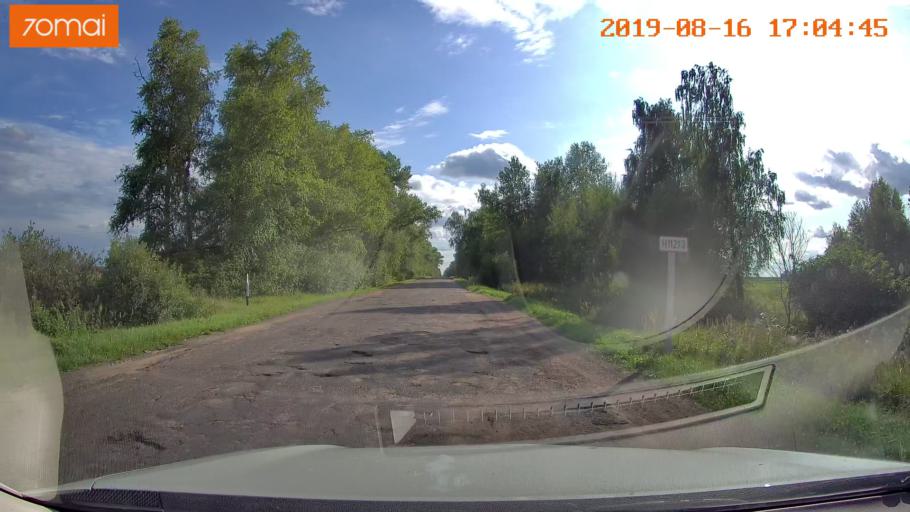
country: BY
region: Mogilev
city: Yalizava
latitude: 53.2421
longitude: 28.9491
